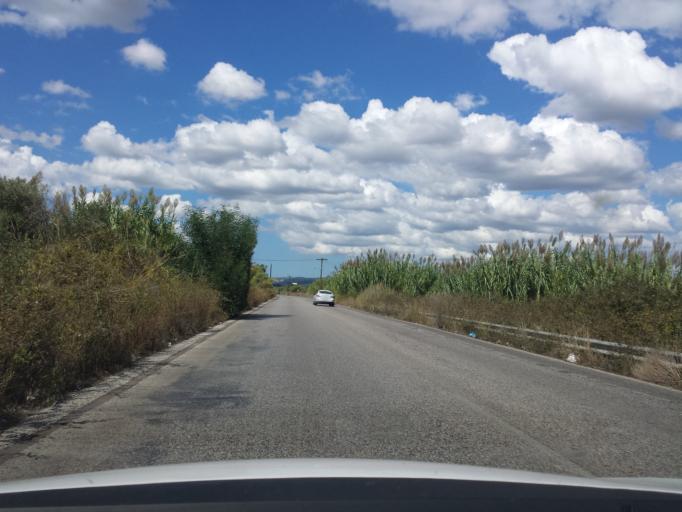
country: GR
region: West Greece
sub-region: Nomos Ileias
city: Epitalion
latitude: 37.6472
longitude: 21.4735
